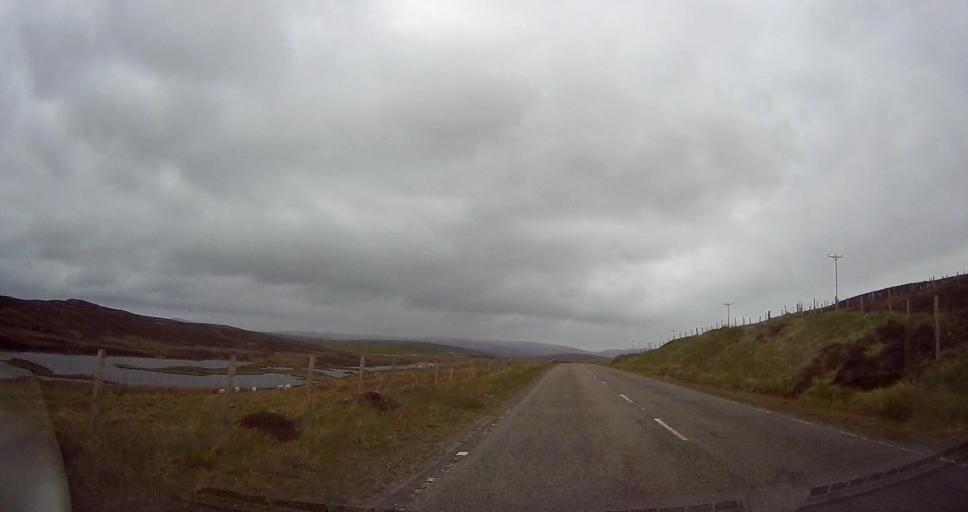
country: GB
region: Scotland
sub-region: Shetland Islands
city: Sandwick
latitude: 60.2583
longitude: -1.4789
